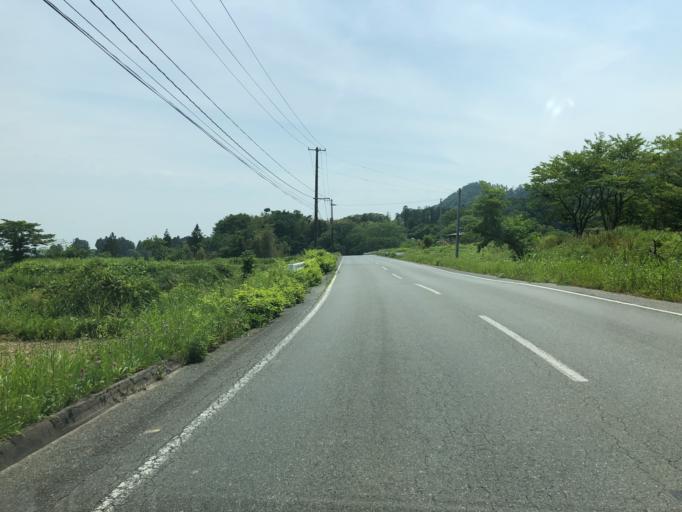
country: JP
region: Fukushima
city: Namie
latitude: 37.5239
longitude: 140.9320
